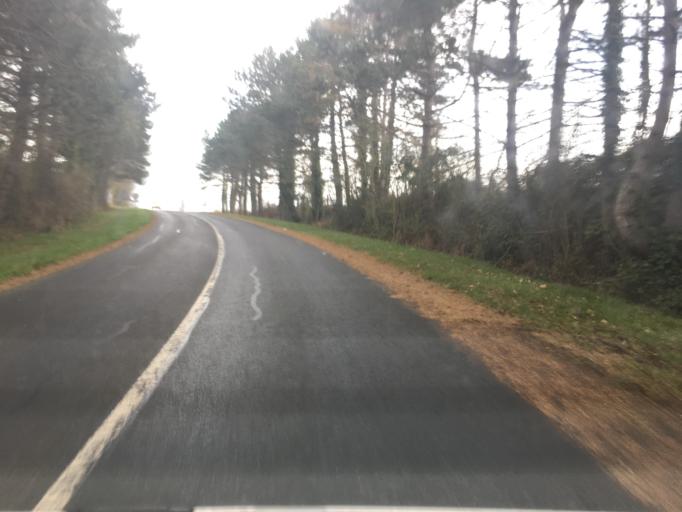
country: FR
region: Lower Normandy
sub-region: Departement du Calvados
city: Saint-Vigor-le-Grand
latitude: 49.3359
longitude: -0.6184
